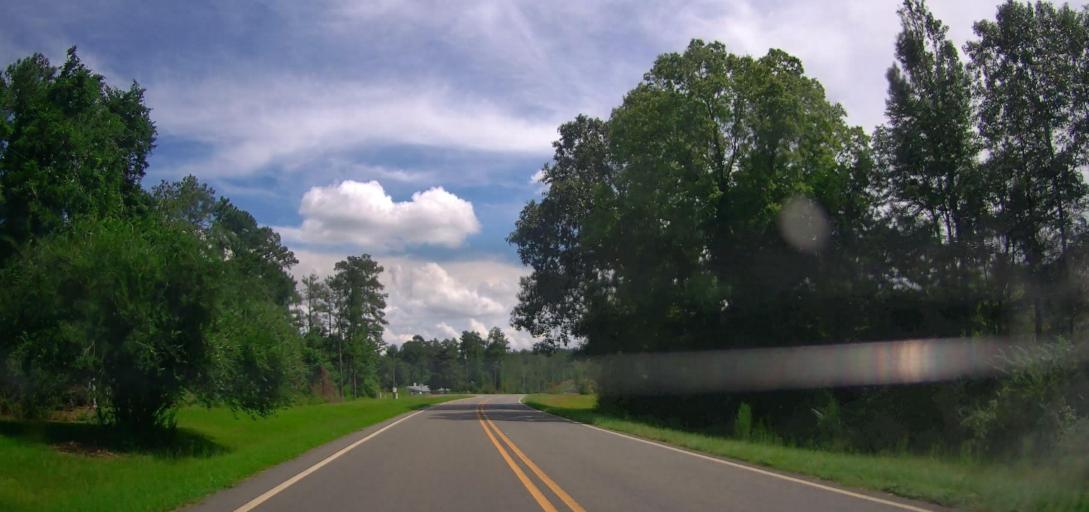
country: US
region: Georgia
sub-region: Taylor County
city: Butler
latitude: 32.5327
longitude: -84.2115
